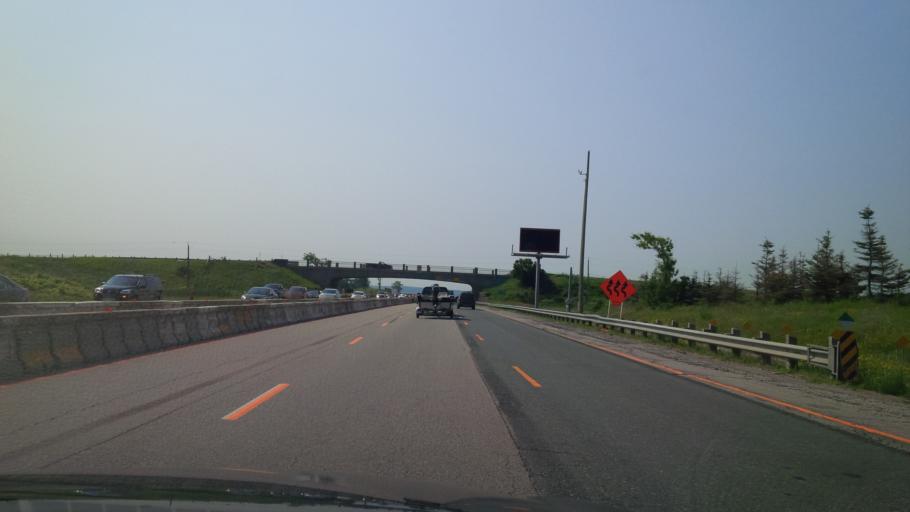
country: CA
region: Ontario
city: Innisfil
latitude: 44.2382
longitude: -79.6673
